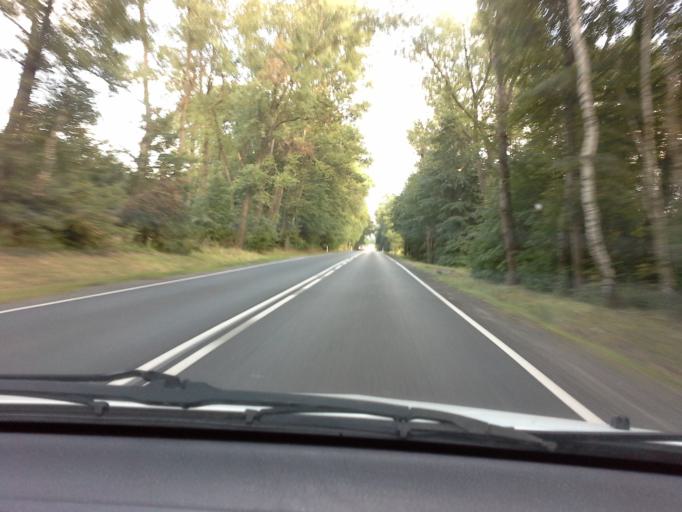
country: PL
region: Lesser Poland Voivodeship
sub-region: Powiat krakowski
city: Filipowice
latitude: 50.1421
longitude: 19.5484
